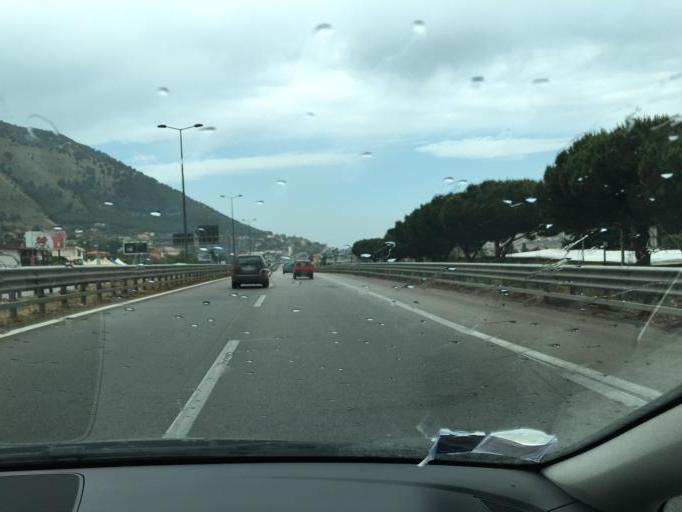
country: IT
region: Sicily
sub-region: Palermo
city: Palermo
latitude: 38.1700
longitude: 13.3007
